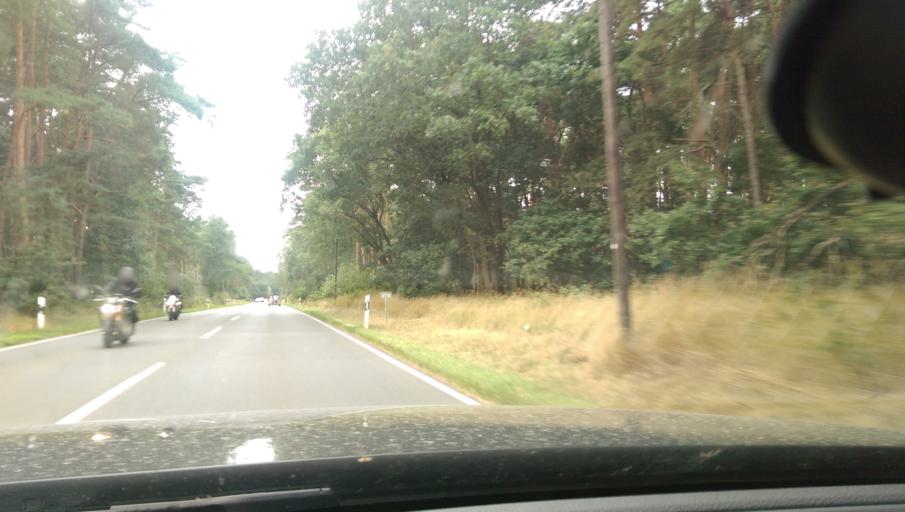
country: DE
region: Lower Saxony
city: Hagenburg
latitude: 52.4850
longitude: 9.2754
